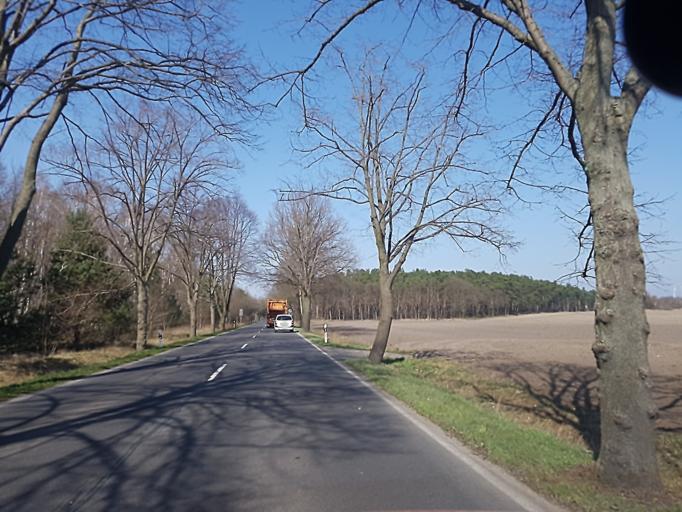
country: DE
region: Brandenburg
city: Forst
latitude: 51.6800
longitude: 14.5979
